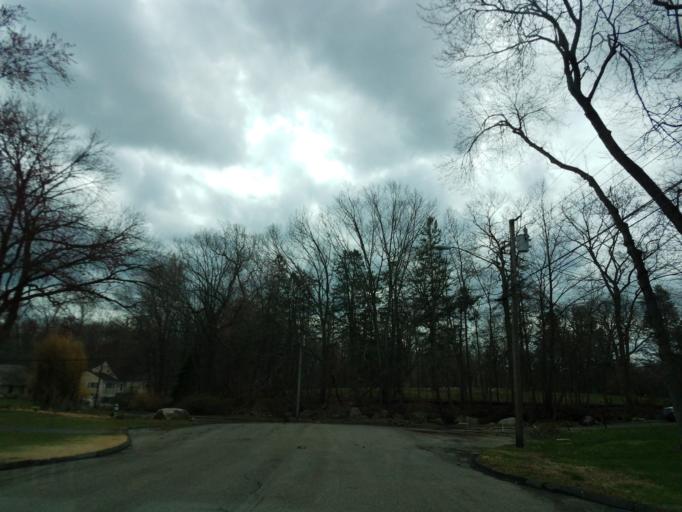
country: US
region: Connecticut
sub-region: Fairfield County
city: Stamford
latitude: 41.0782
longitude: -73.5391
